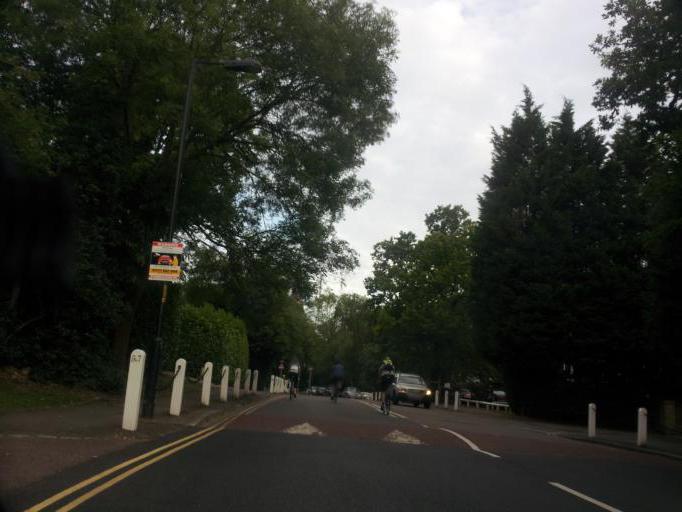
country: GB
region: England
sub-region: Greater London
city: Thornton Heath
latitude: 51.4340
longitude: -0.0794
